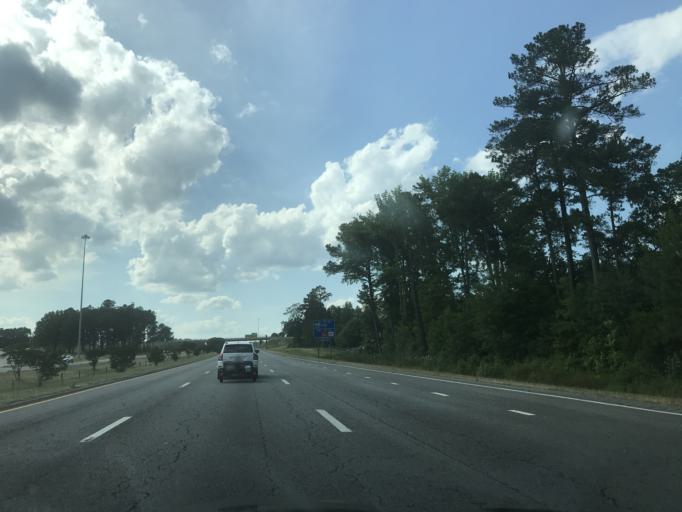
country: US
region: North Carolina
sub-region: Nash County
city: Rocky Mount
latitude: 35.9735
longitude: -77.8435
